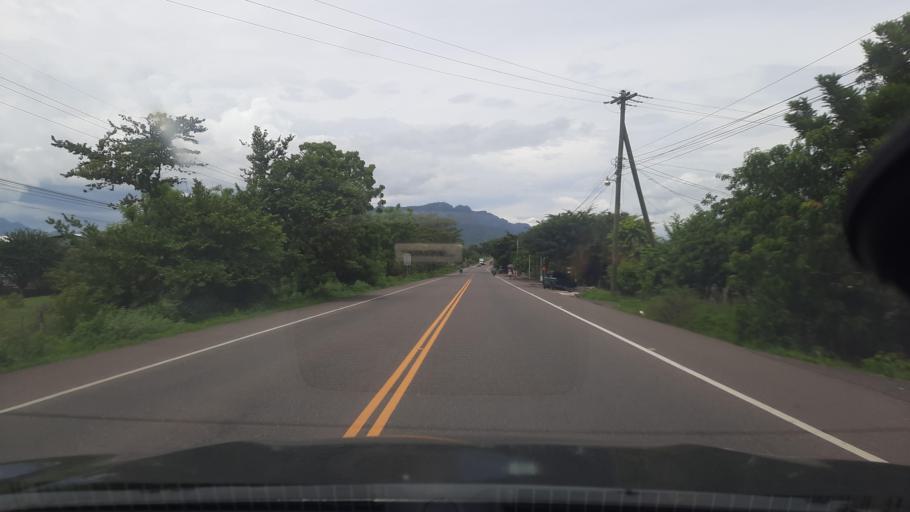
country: HN
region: Valle
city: Jicaro Galan
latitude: 13.5328
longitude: -87.4568
